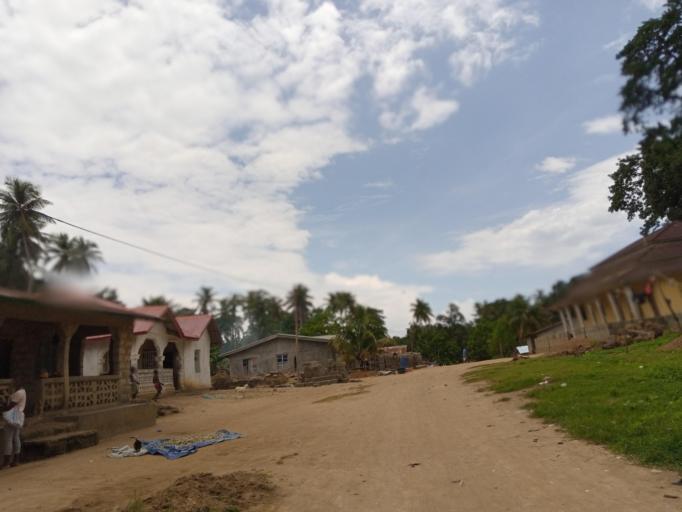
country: SL
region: Northern Province
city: Masoyila
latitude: 8.5599
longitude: -13.1721
